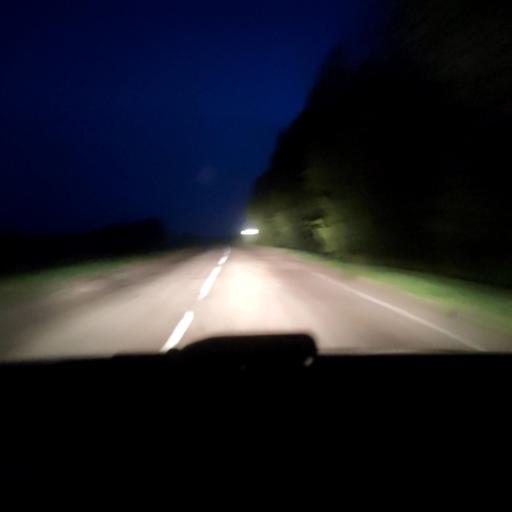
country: RU
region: Voronezj
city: Kashirskoye
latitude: 51.5467
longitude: 39.8459
